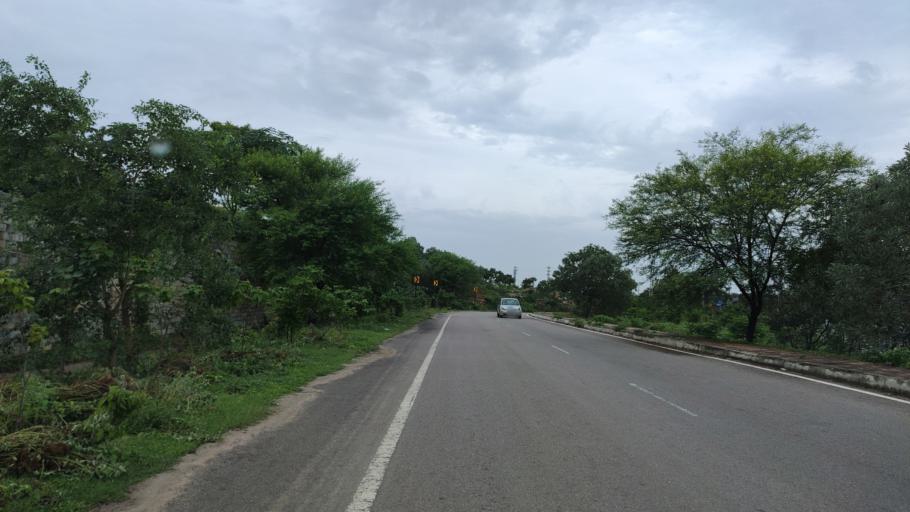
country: IN
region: Telangana
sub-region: Rangareddi
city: Secunderabad
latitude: 17.5784
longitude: 78.5768
